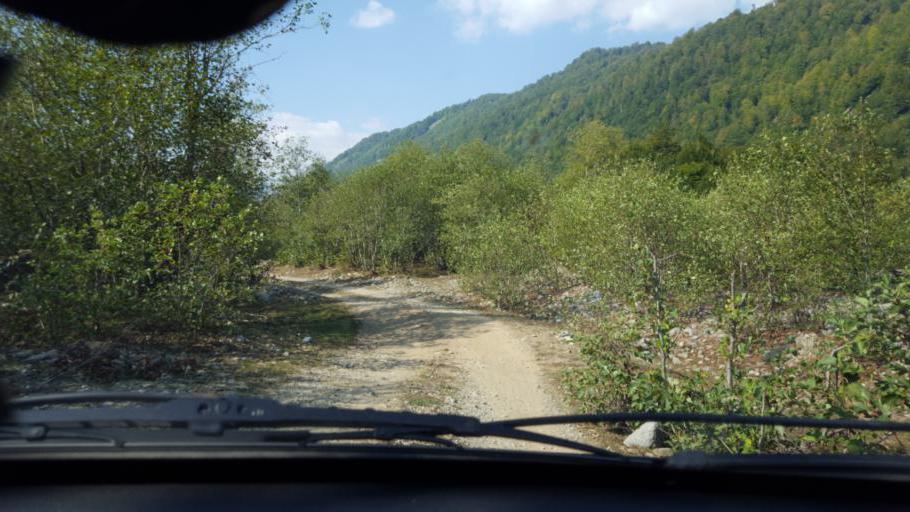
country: ME
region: Andrijevica
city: Andrijevica
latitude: 42.5946
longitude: 19.6501
